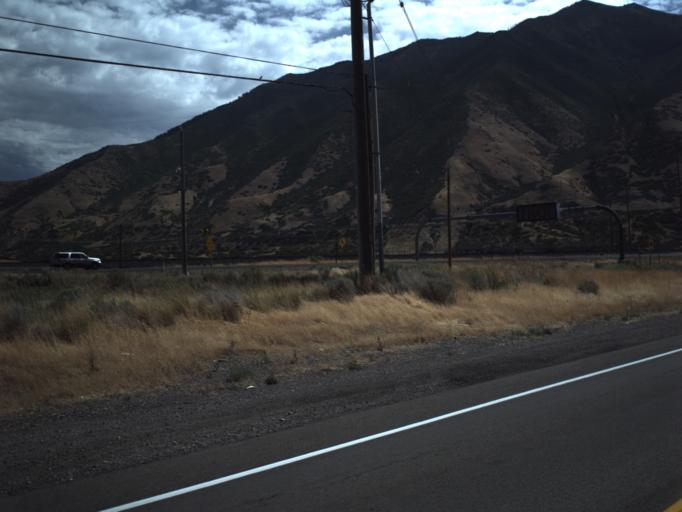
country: US
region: Utah
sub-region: Utah County
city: Mapleton
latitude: 40.0907
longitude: -111.5983
